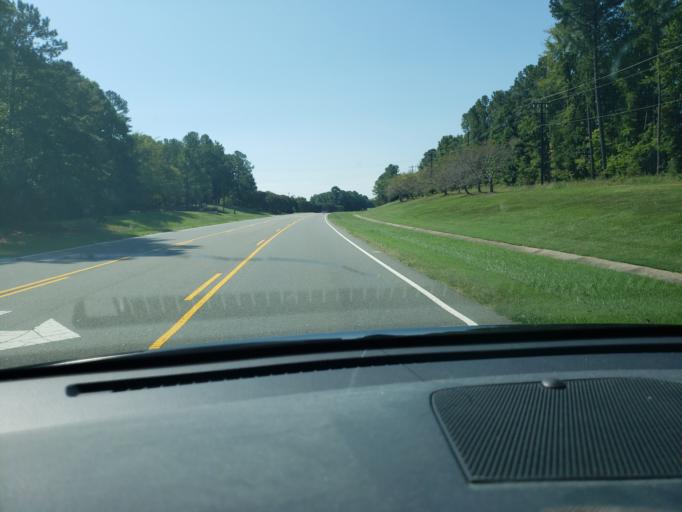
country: US
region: North Carolina
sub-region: Durham County
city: Durham
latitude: 35.9092
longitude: -78.8779
